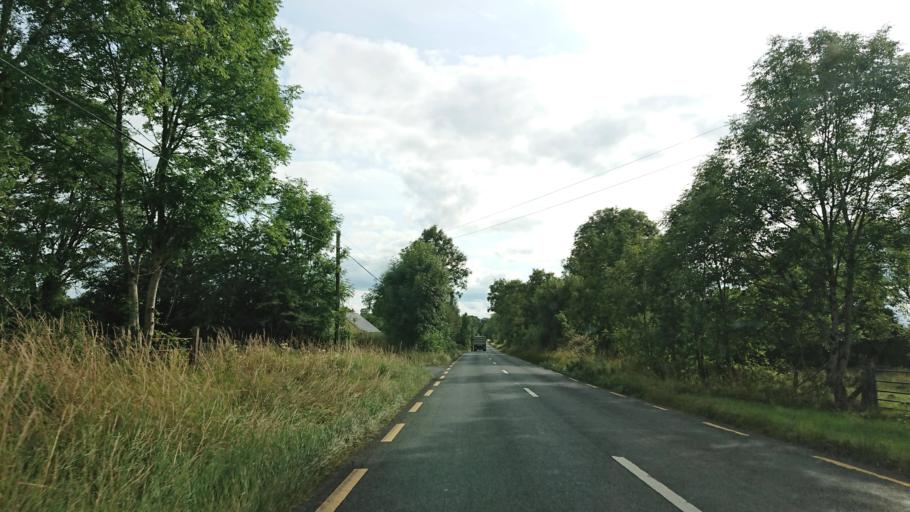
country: IE
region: Connaught
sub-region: County Leitrim
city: Carrick-on-Shannon
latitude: 53.9708
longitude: -8.0650
